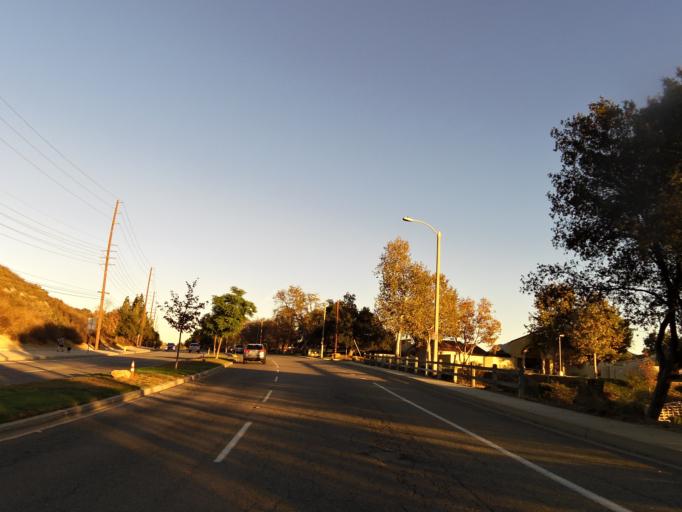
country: US
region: California
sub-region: Los Angeles County
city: Westlake Village
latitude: 34.1567
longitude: -118.8111
